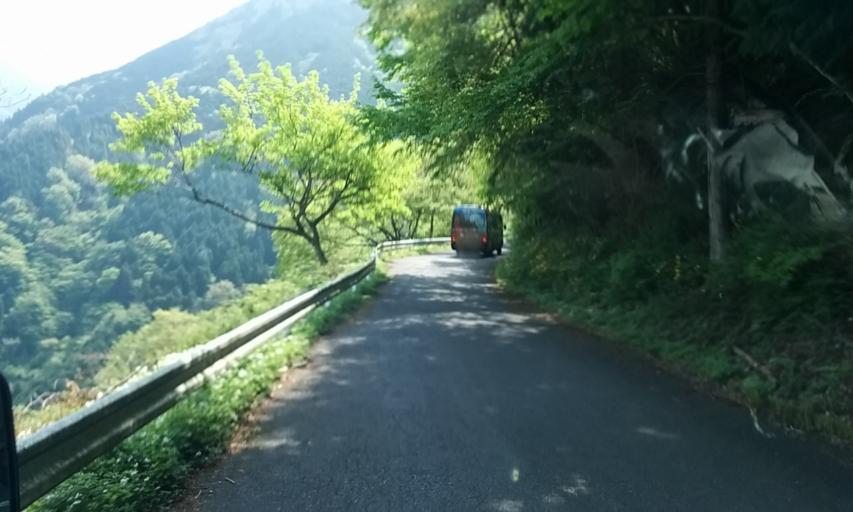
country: JP
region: Ehime
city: Niihama
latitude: 33.8750
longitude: 133.3018
